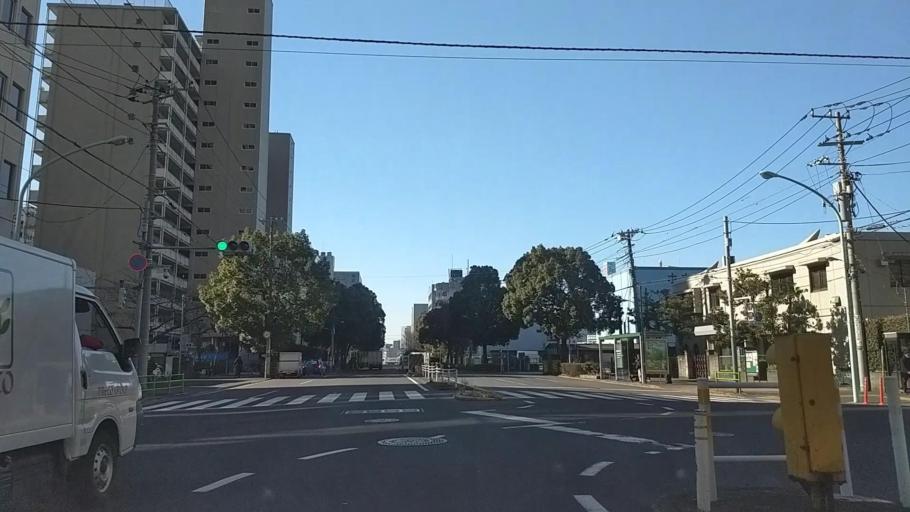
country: JP
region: Tokyo
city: Tokyo
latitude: 35.6551
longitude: 139.7715
